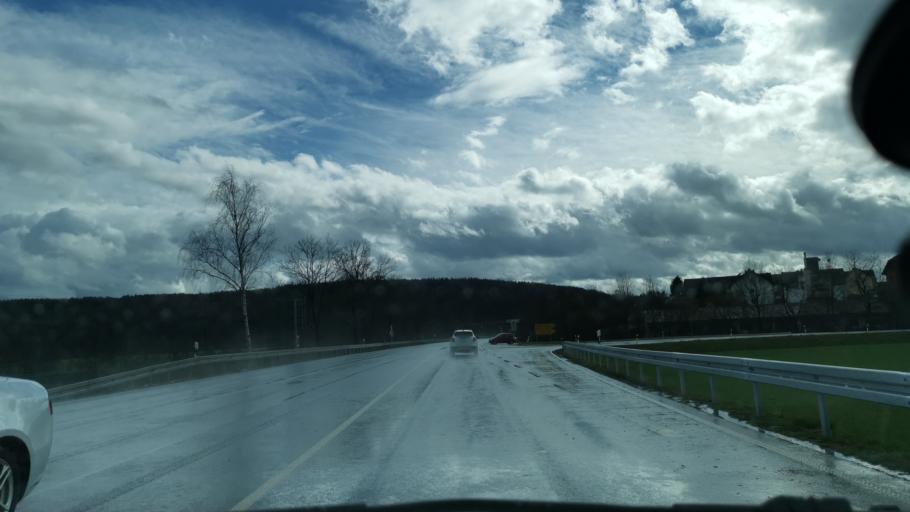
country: DE
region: Hesse
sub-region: Regierungsbezirk Kassel
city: Bad Hersfeld
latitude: 50.9062
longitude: 9.7488
